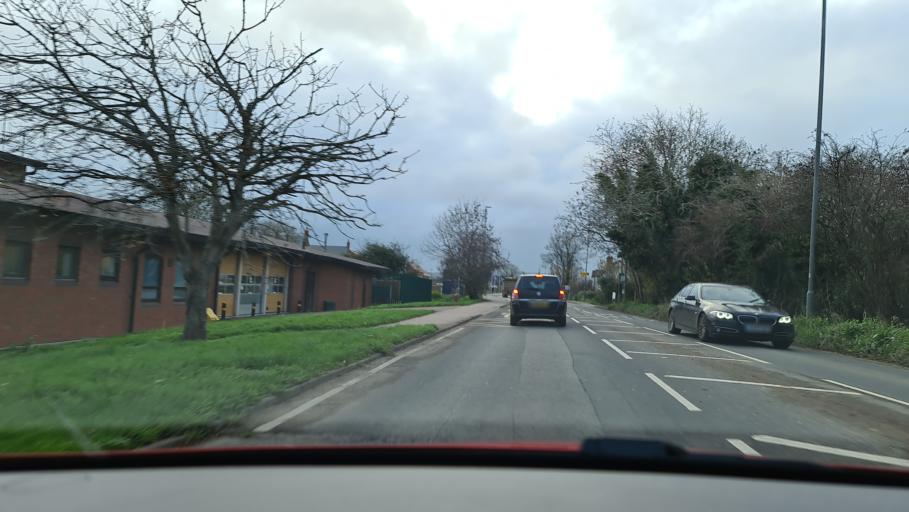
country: GB
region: England
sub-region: Buckinghamshire
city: Aylesbury
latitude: 51.7965
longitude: -0.8046
